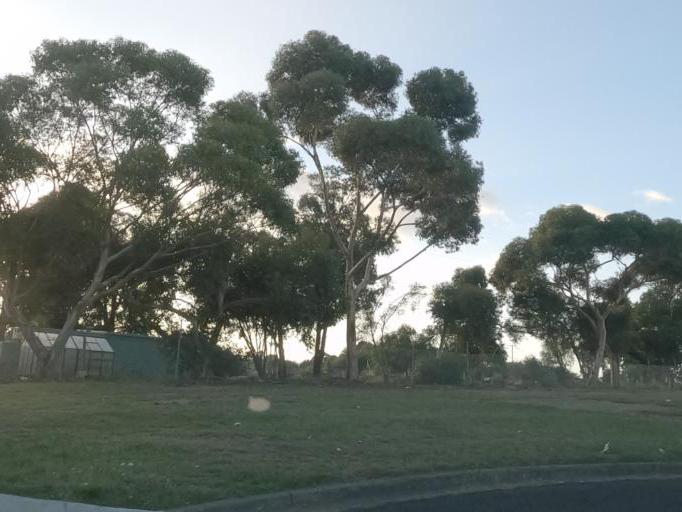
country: AU
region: Victoria
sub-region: Hume
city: Jacana
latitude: -37.6759
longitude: 144.9051
